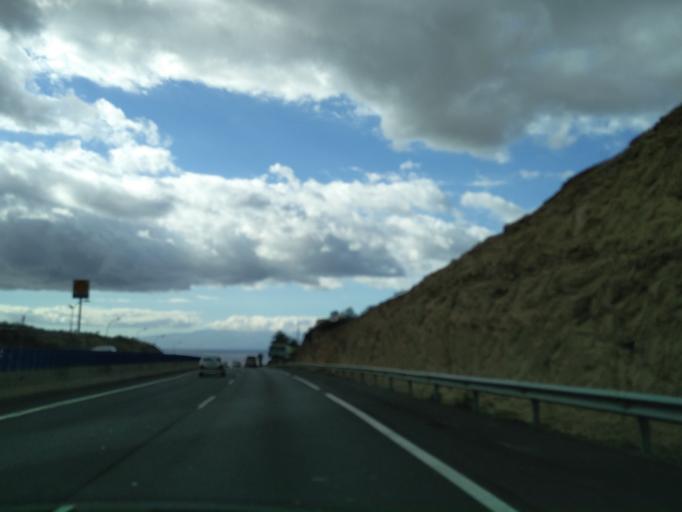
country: ES
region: Canary Islands
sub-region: Provincia de Santa Cruz de Tenerife
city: Playa de las Americas
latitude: 28.0596
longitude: -16.6910
